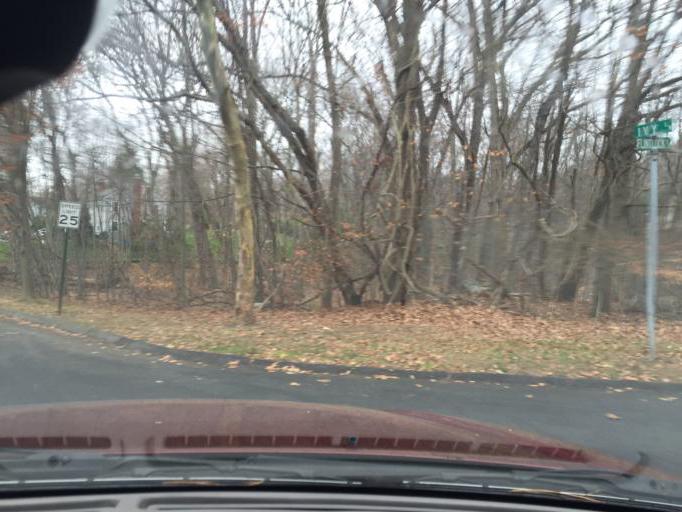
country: US
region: Connecticut
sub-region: Fairfield County
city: Southport
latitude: 41.1451
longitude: -73.2933
